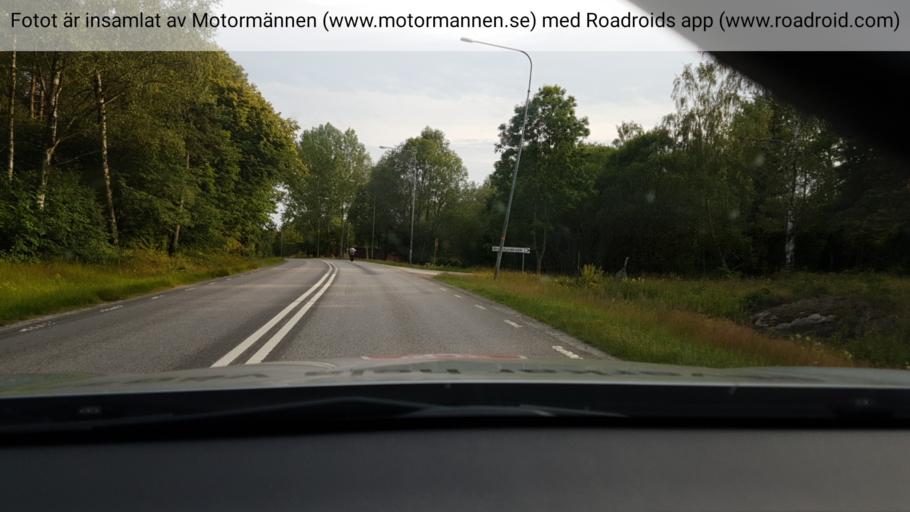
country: SE
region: Vaestra Goetaland
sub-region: Uddevalla Kommun
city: Uddevalla
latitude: 58.3666
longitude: 11.9677
